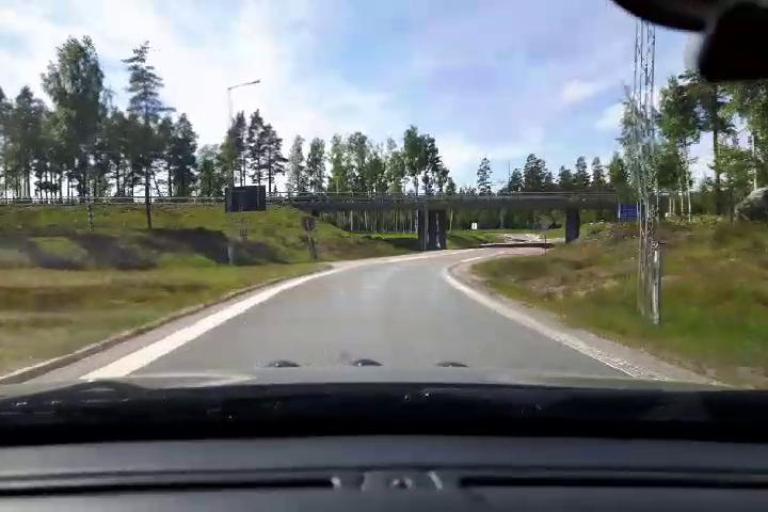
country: SE
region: Gaevleborg
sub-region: Gavle Kommun
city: Norrsundet
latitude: 61.0719
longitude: 16.9654
